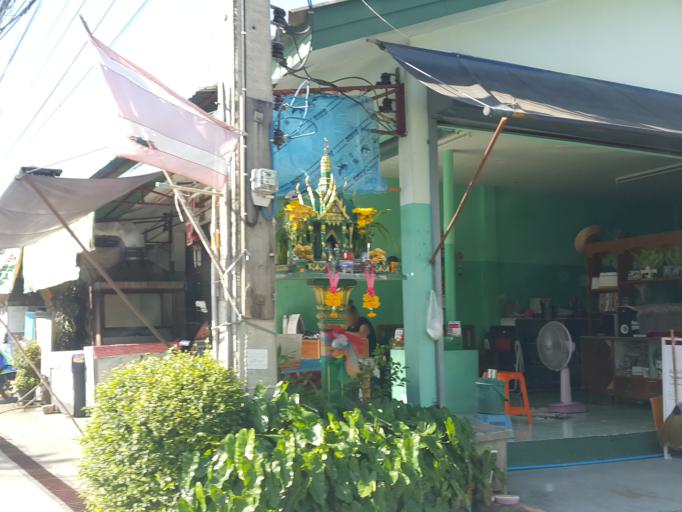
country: TH
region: Chiang Mai
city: Saraphi
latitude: 18.7765
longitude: 99.0529
